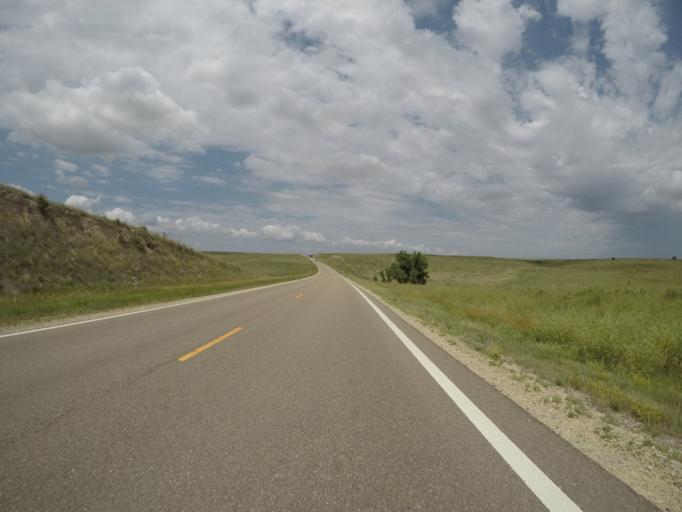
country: US
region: Kansas
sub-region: Rawlins County
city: Atwood
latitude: 39.7528
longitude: -101.0473
